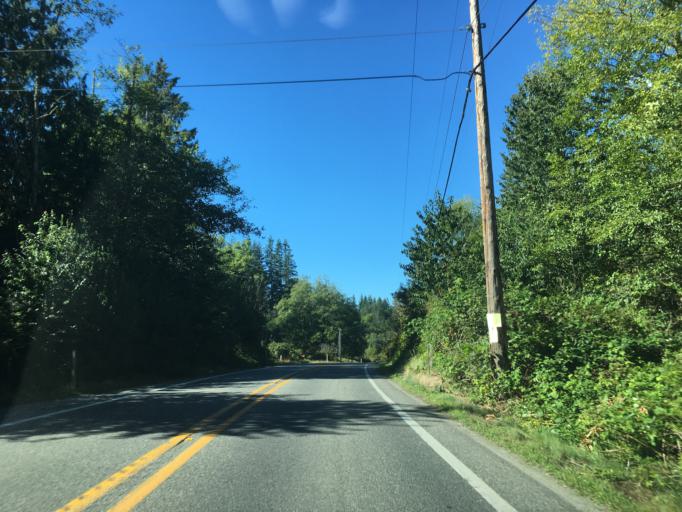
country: US
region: Washington
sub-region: Skagit County
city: Sedro-Woolley
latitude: 48.5576
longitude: -122.2253
